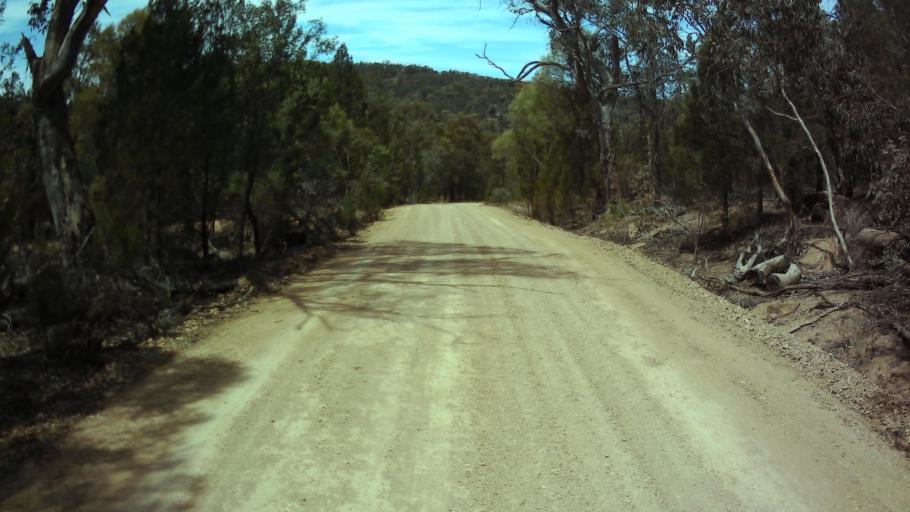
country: AU
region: New South Wales
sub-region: Weddin
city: Grenfell
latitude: -33.8120
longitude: 148.1604
